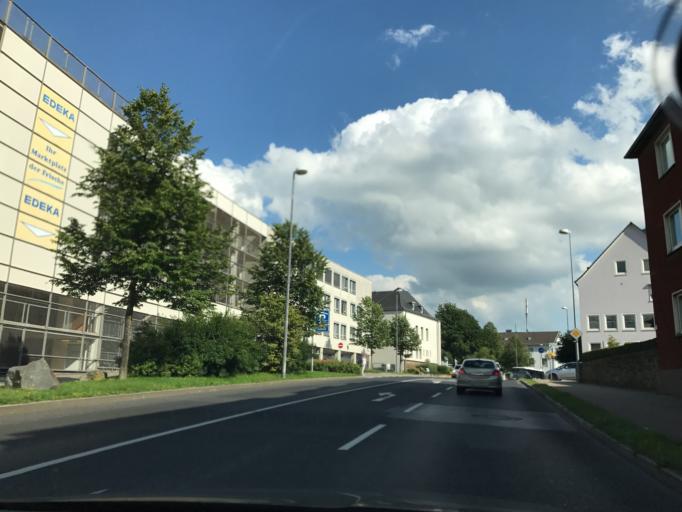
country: DE
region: North Rhine-Westphalia
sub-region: Regierungsbezirk Dusseldorf
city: Velbert
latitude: 51.3410
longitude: 7.0401
